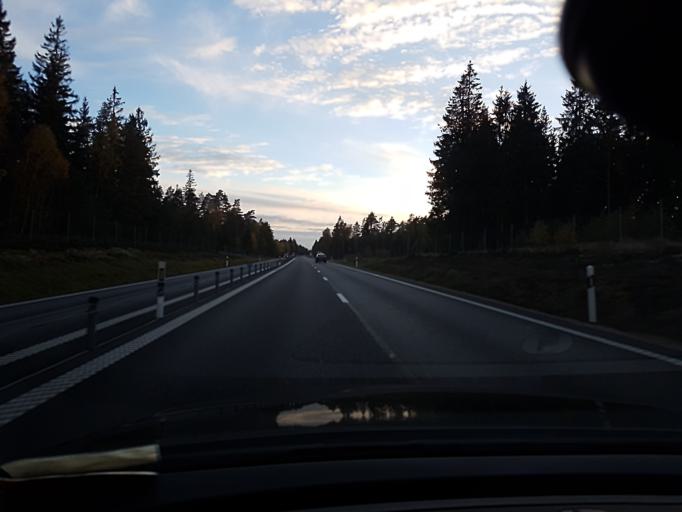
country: SE
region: Kronoberg
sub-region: Ljungby Kommun
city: Ljungby
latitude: 56.7810
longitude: 13.8199
